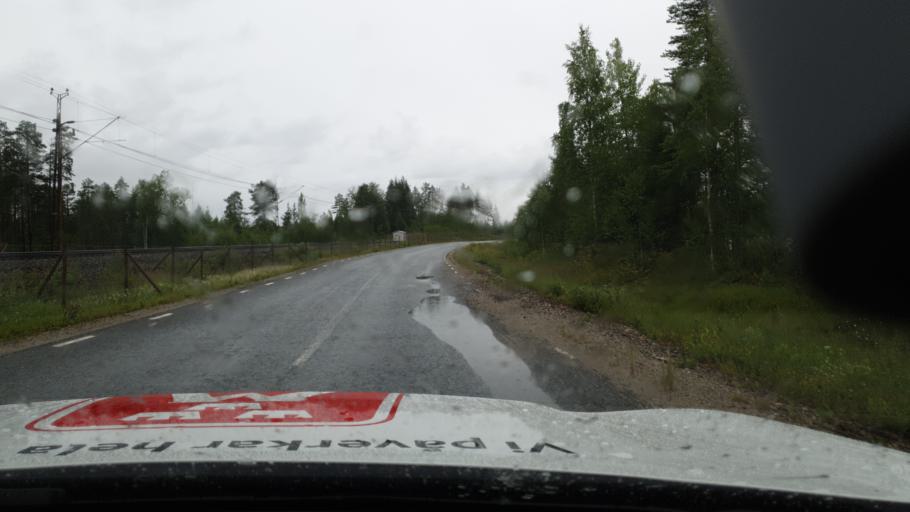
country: SE
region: Vaesterbotten
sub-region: Vindelns Kommun
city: Vindeln
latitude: 64.4510
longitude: 19.7470
